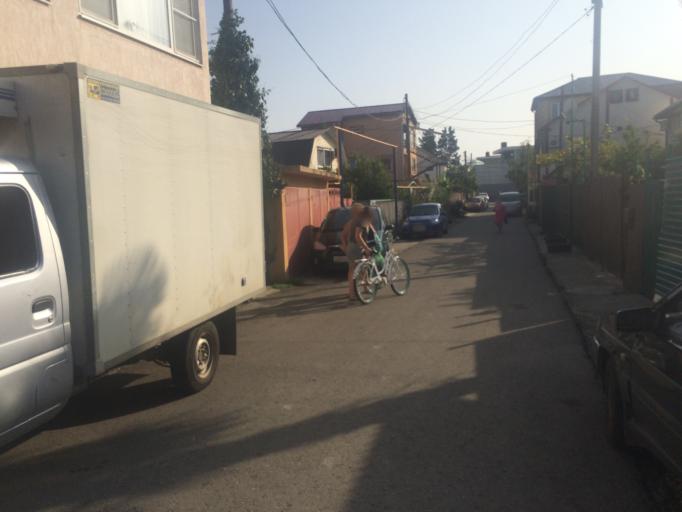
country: RU
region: Krasnodarskiy
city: Adler
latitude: 43.3928
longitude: 39.9795
